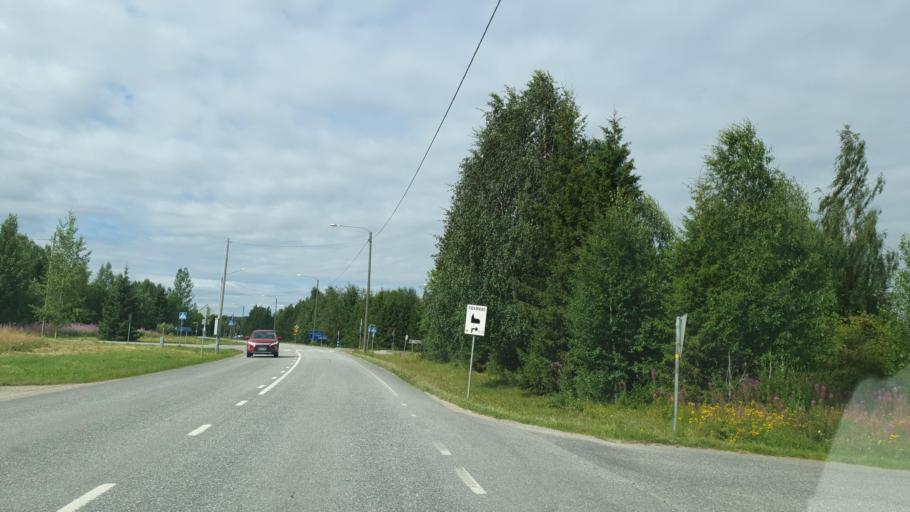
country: FI
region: Lapland
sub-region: Tunturi-Lappi
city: Kittilae
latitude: 67.6471
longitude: 24.9271
